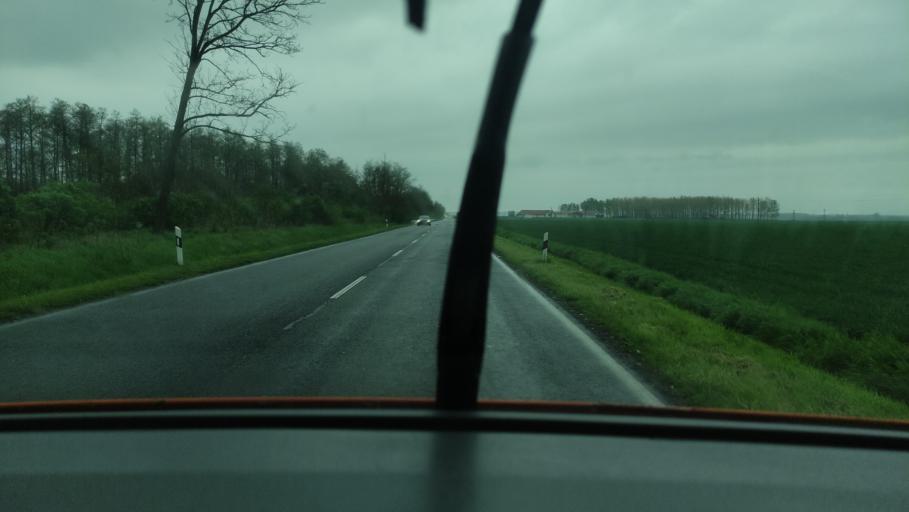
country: HU
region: Baranya
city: Mohacs
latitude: 45.9345
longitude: 18.6617
